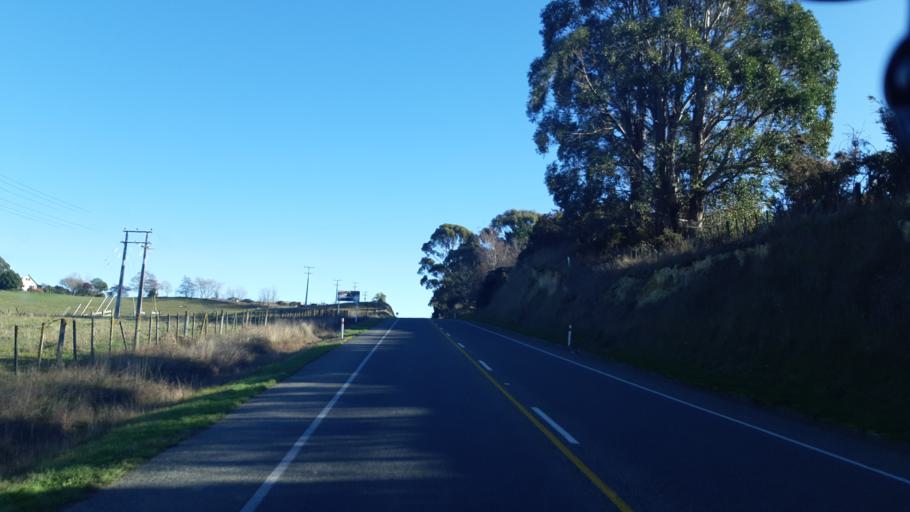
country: NZ
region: Tasman
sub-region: Tasman District
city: Mapua
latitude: -41.2985
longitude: 173.1051
